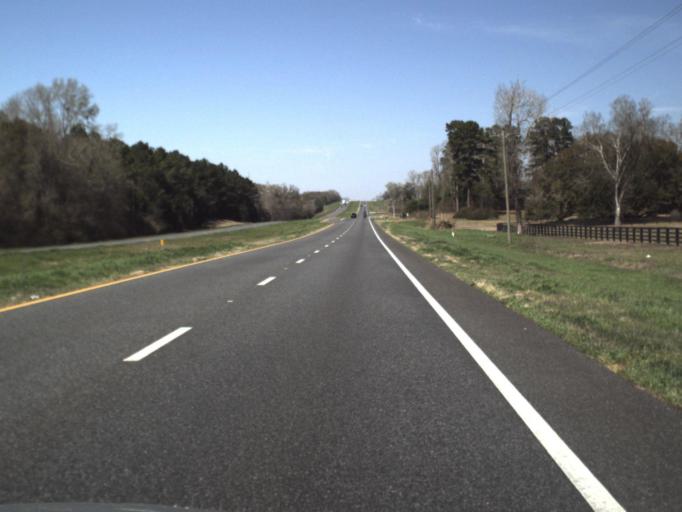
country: US
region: Florida
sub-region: Jackson County
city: Marianna
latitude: 30.8749
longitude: -85.3618
